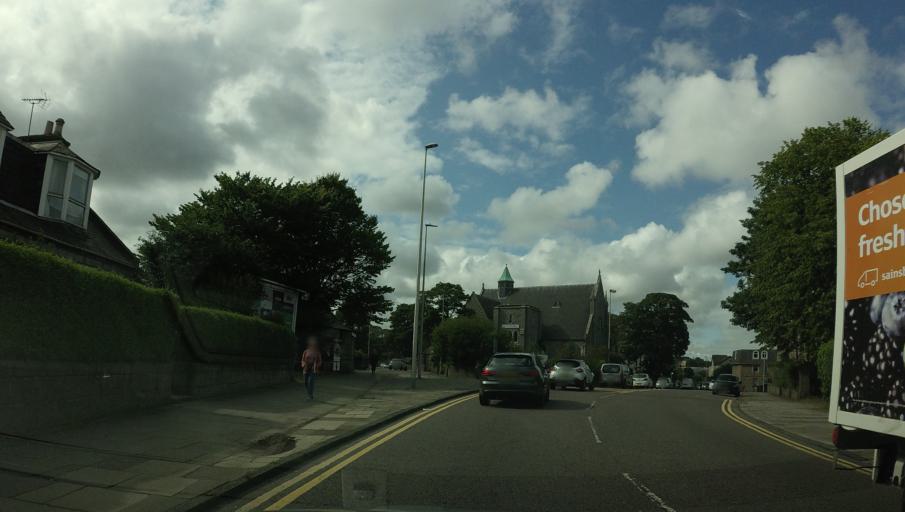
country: GB
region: Scotland
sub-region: Aberdeen City
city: Aberdeen
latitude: 57.1524
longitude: -2.1112
